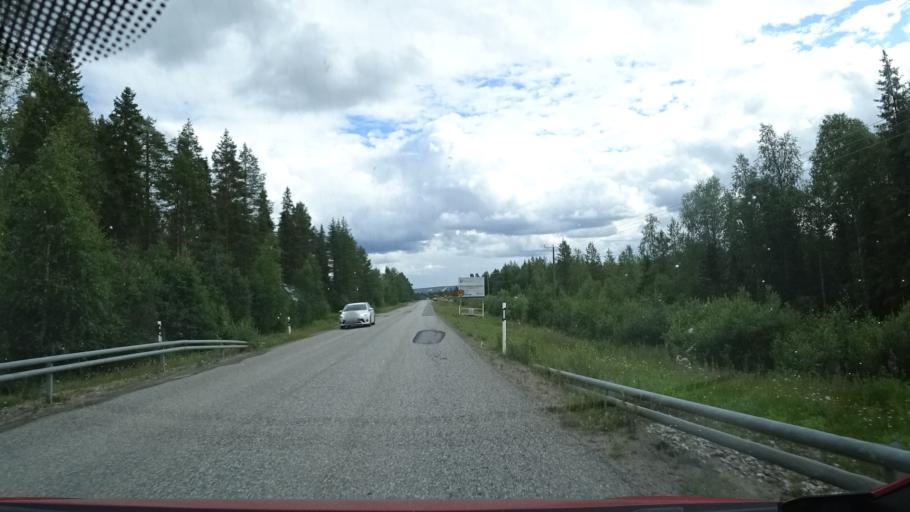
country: FI
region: Lapland
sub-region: Rovaniemi
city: Rovaniemi
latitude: 66.5449
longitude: 25.7088
